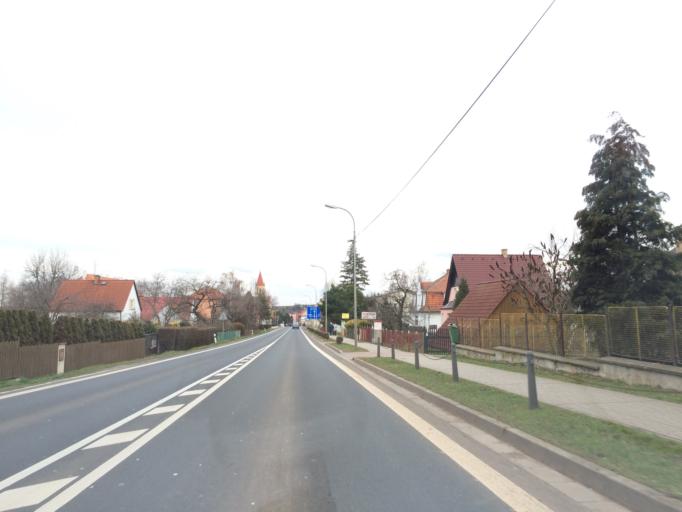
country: CZ
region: Ustecky
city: Lubenec
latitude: 50.1320
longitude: 13.3097
